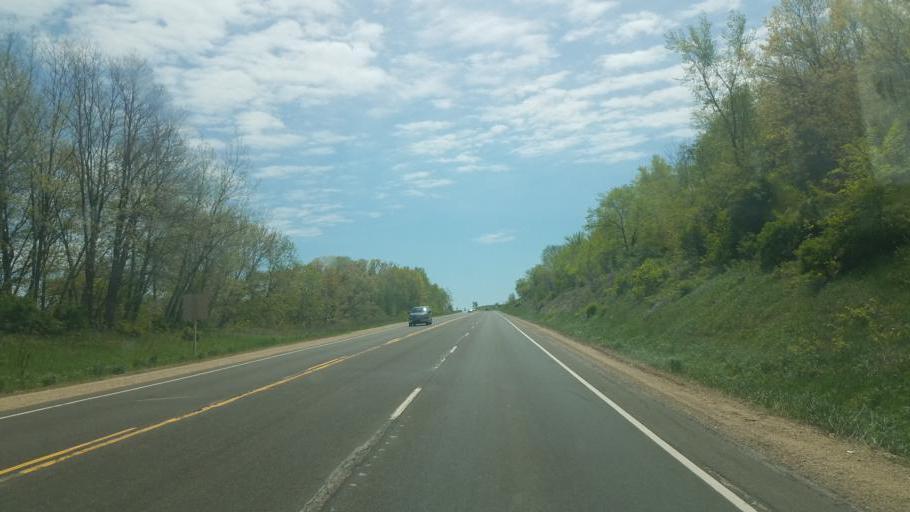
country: US
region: Wisconsin
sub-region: Monroe County
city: Tomah
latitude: 43.9077
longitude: -90.4931
